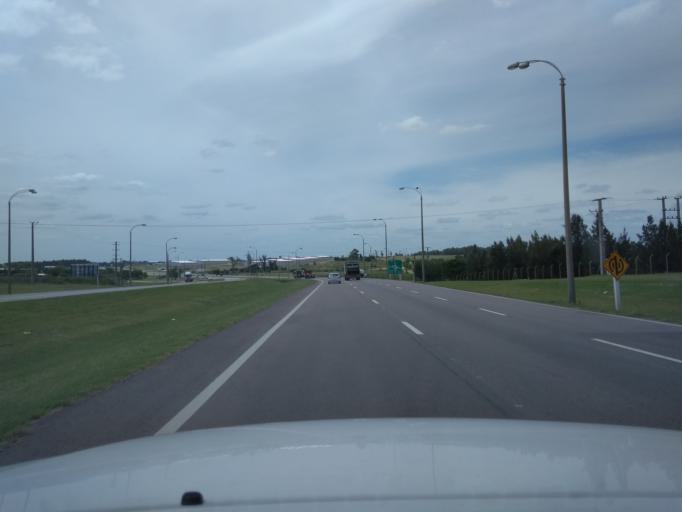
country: UY
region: Canelones
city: Las Piedras
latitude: -34.6979
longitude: -56.2386
